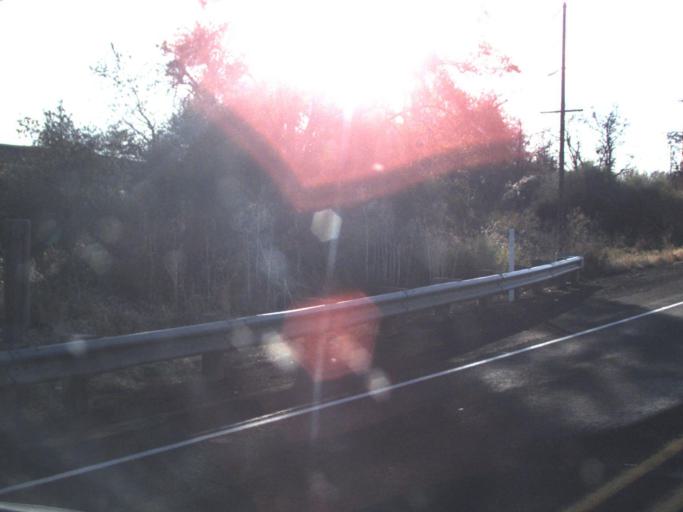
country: US
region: Washington
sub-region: Walla Walla County
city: Waitsburg
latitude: 46.1366
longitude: -118.1675
